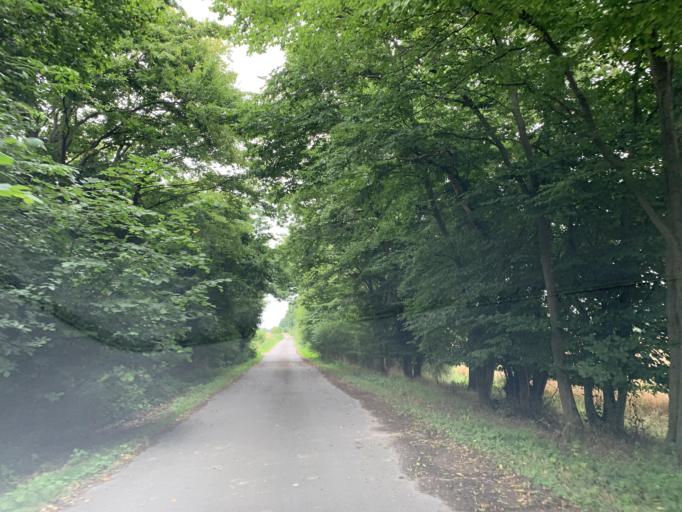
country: DE
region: Mecklenburg-Vorpommern
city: Blankensee
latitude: 53.4226
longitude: 13.2701
